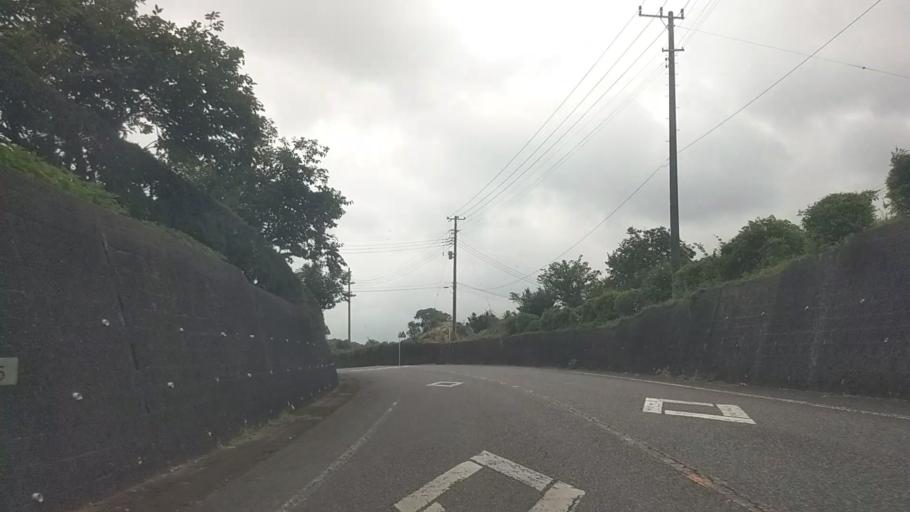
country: JP
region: Chiba
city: Kimitsu
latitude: 35.2493
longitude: 139.9985
